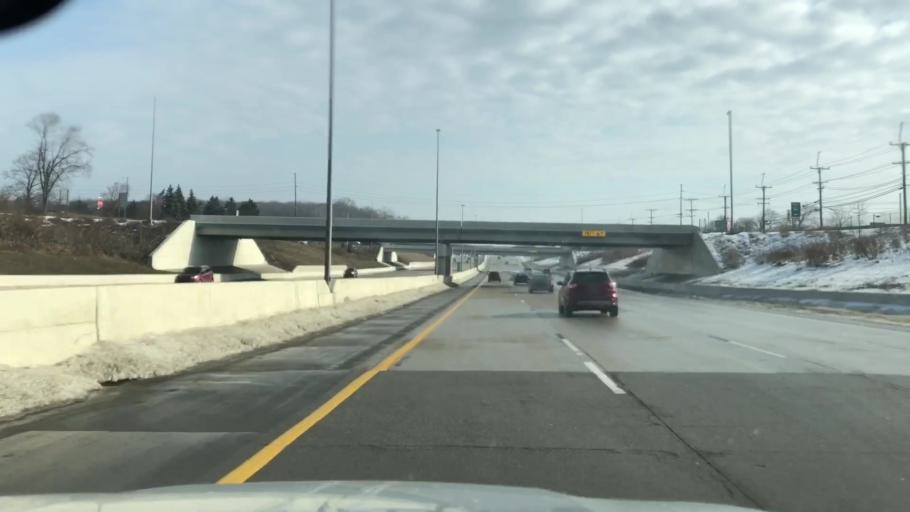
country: US
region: Michigan
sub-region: Wayne County
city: Plymouth
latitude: 42.3808
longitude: -83.4157
